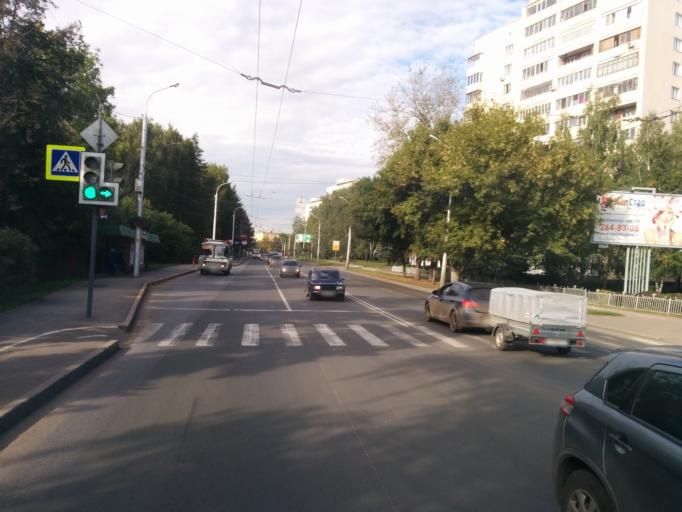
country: RU
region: Bashkortostan
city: Ufa
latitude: 54.8129
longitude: 56.0566
